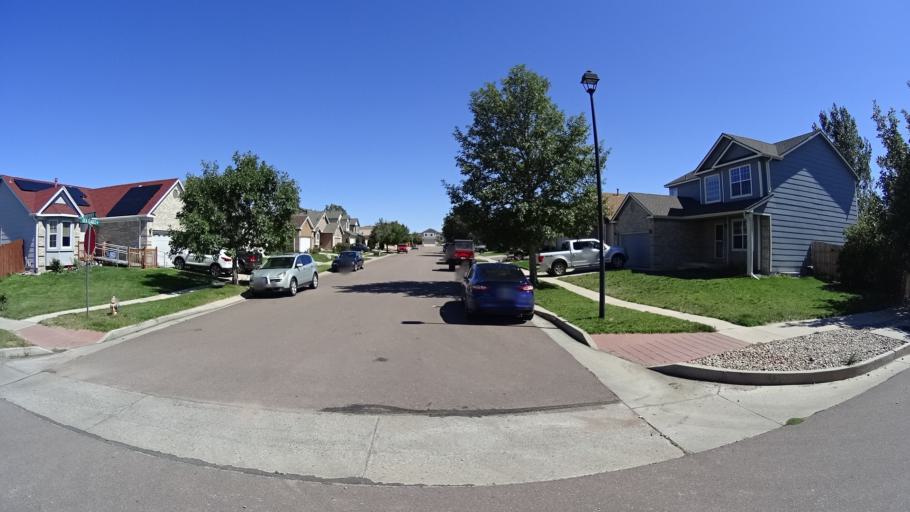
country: US
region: Colorado
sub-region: El Paso County
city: Stratmoor
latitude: 38.7873
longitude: -104.7364
